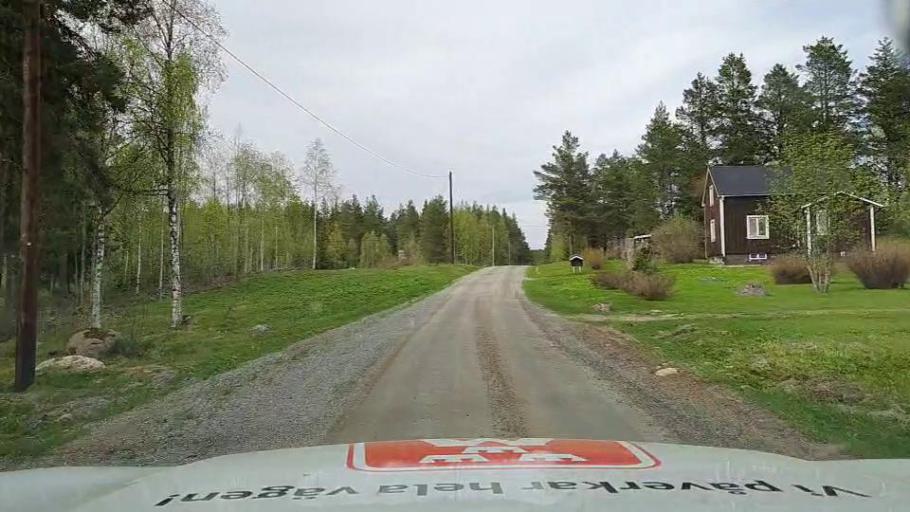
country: SE
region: Jaemtland
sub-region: OEstersunds Kommun
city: Brunflo
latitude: 62.5923
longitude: 14.9110
